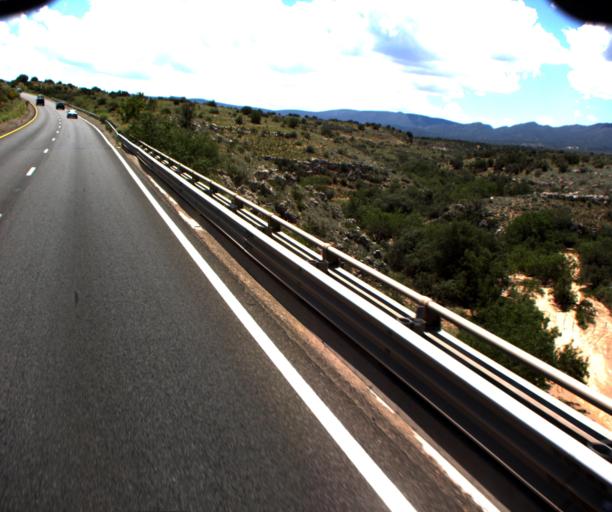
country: US
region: Arizona
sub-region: Yavapai County
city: Verde Village
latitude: 34.6685
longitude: -111.9699
